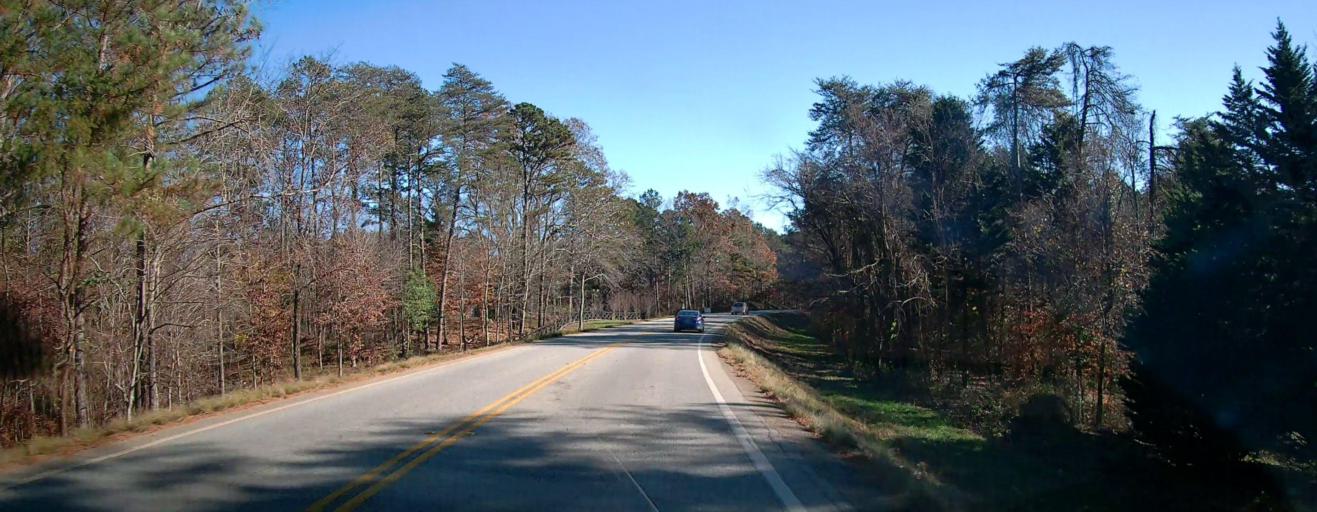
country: US
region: Georgia
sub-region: Hall County
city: Lula
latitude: 34.4416
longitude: -83.7195
